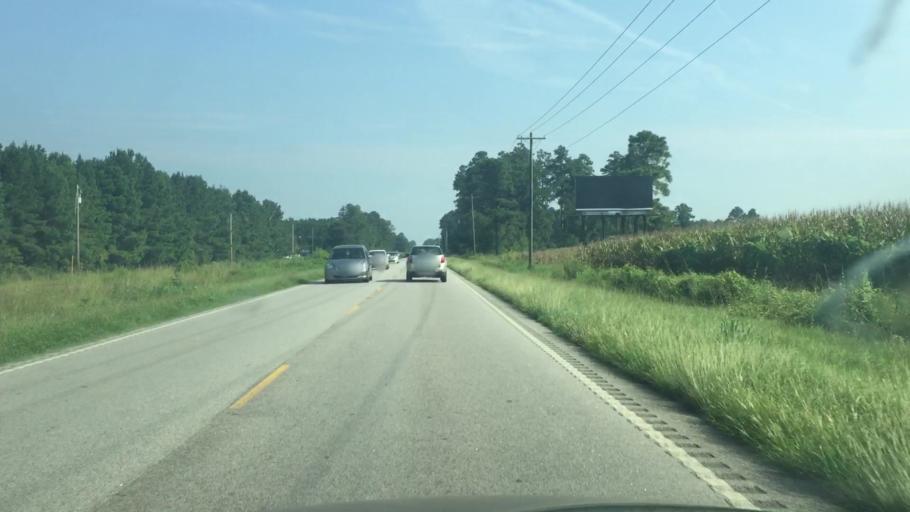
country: US
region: North Carolina
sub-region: Columbus County
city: Tabor City
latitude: 34.1186
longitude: -78.8758
